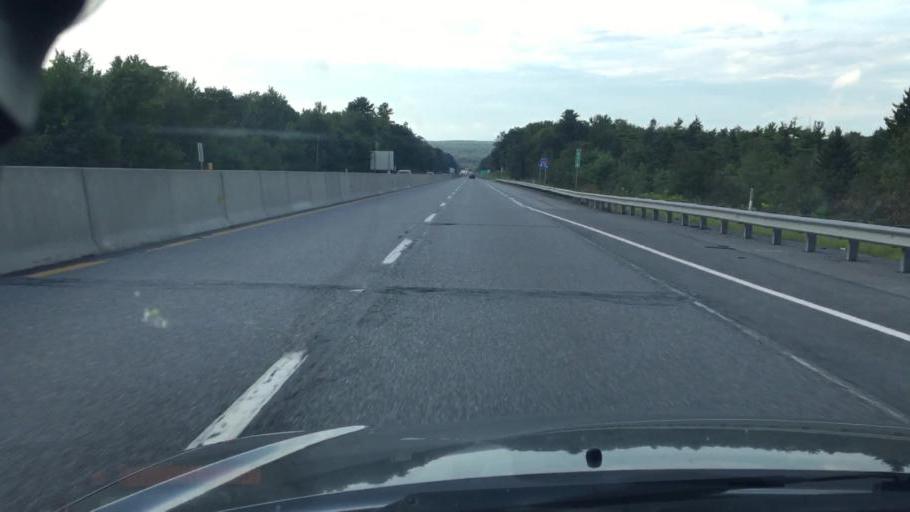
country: US
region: Pennsylvania
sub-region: Carbon County
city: Towamensing Trails
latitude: 40.9906
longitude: -75.6314
